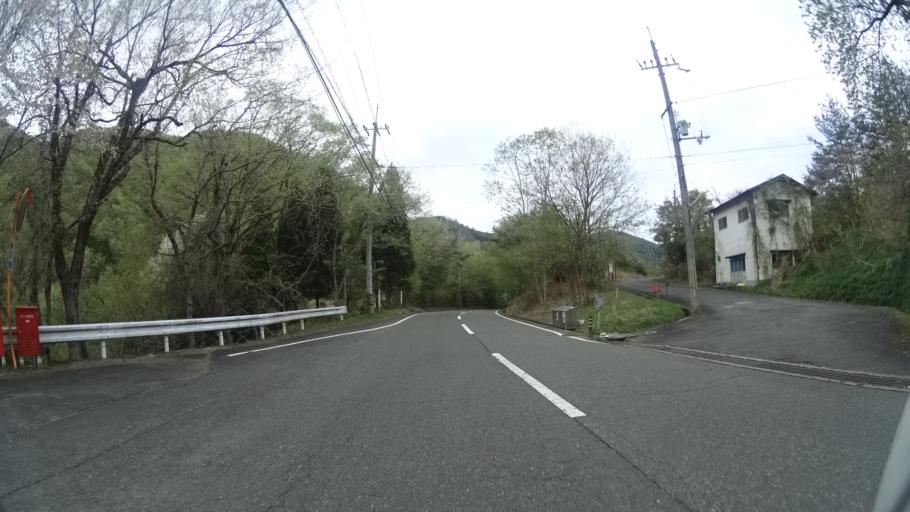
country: JP
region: Kyoto
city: Ayabe
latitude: 35.2113
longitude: 135.4599
